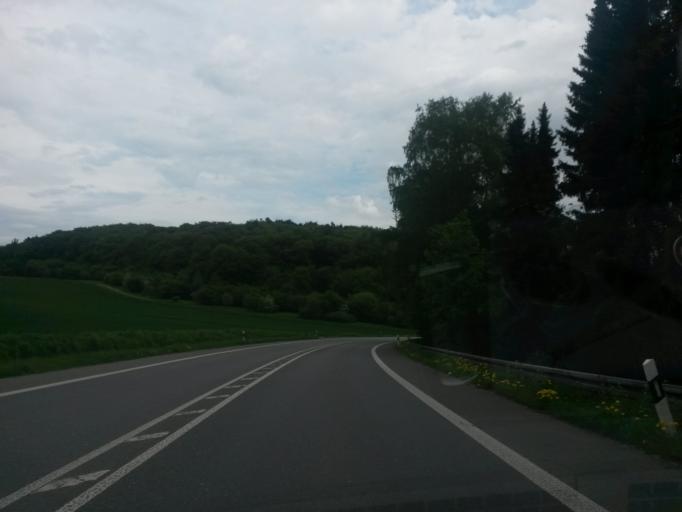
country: DE
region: North Rhine-Westphalia
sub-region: Regierungsbezirk Arnsberg
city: Hagen
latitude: 51.3557
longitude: 7.5468
